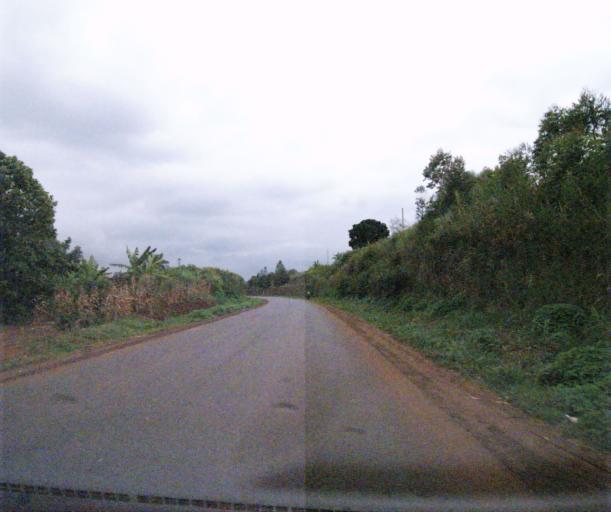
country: CM
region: West
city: Bansoa
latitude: 5.4847
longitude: 10.2146
